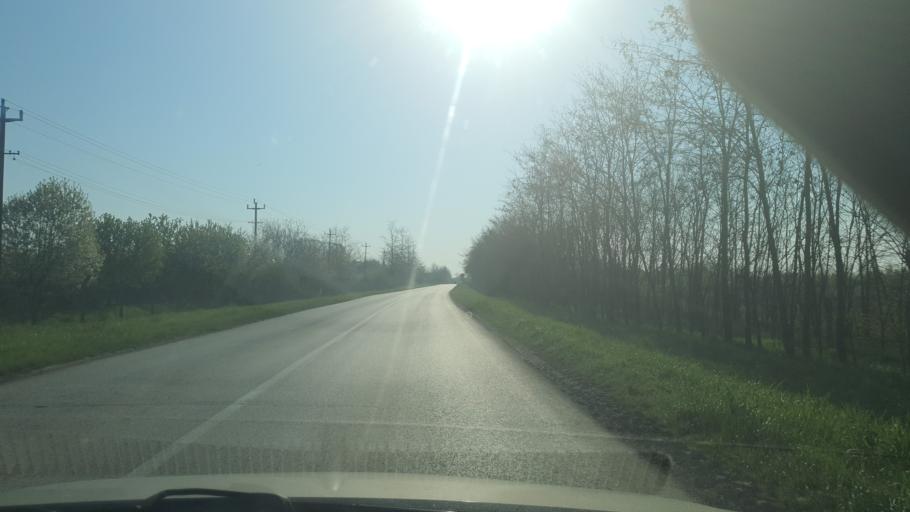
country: RS
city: Zmajevo
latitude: 45.4590
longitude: 19.6603
